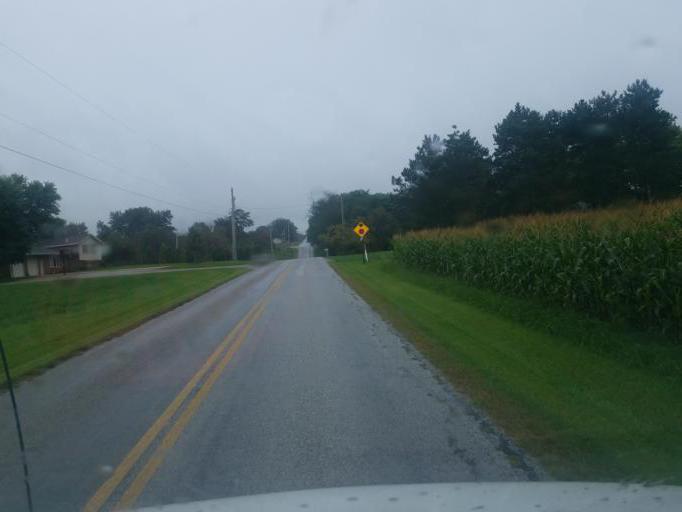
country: US
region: Ohio
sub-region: Wayne County
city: Rittman
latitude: 40.9777
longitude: -81.8031
